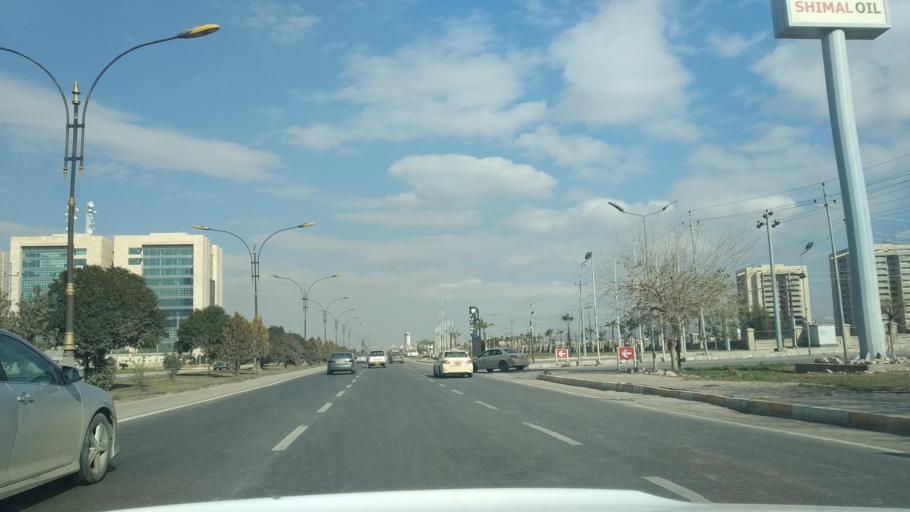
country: IQ
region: Arbil
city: Erbil
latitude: 36.2453
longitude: 44.0702
